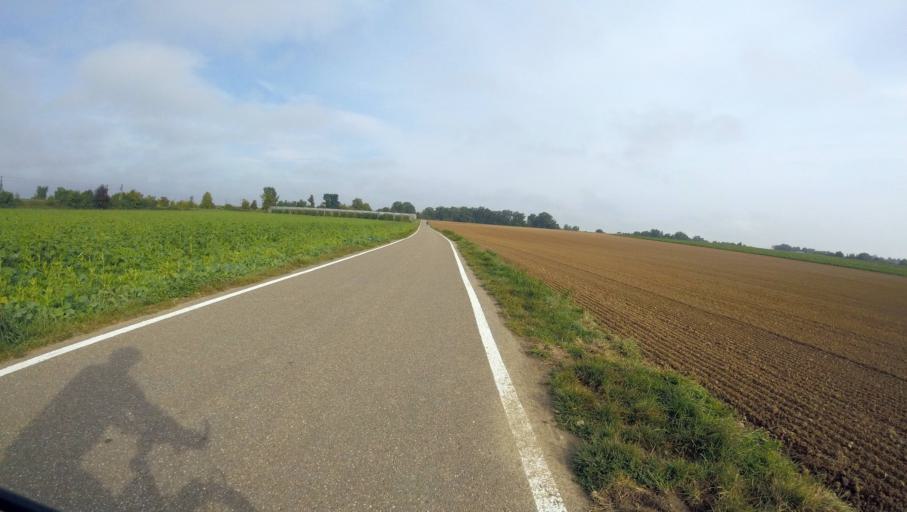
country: DE
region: Baden-Wuerttemberg
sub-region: Regierungsbezirk Stuttgart
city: Bondorf
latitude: 48.5286
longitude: 8.8290
